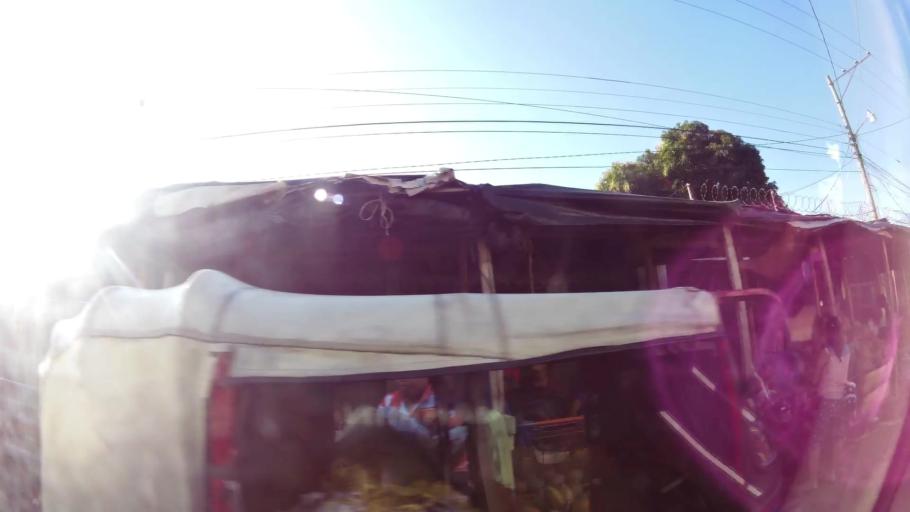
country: GT
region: Suchitepeque
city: Mazatenango
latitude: 14.5326
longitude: -91.5077
